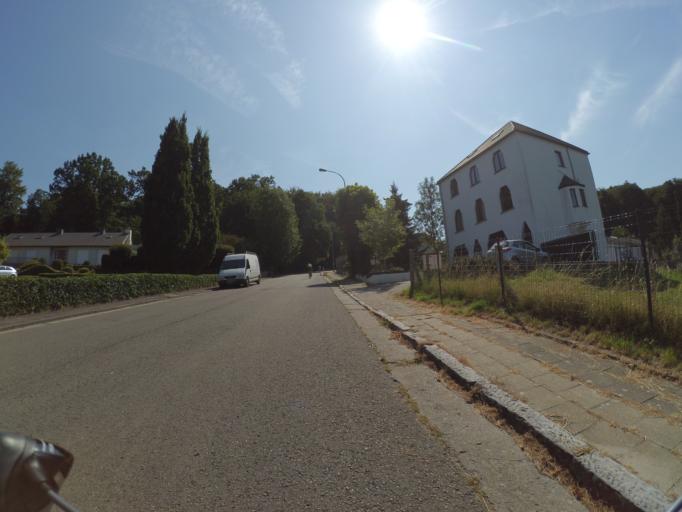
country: BE
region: Flanders
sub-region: Provincie West-Vlaanderen
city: Avelgem
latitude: 50.7615
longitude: 3.4846
